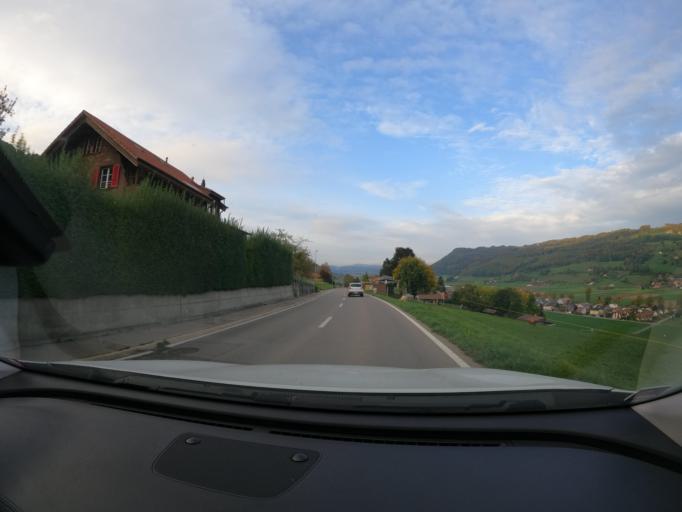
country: CH
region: Bern
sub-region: Bern-Mittelland District
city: Toffen
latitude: 46.8533
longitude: 7.4909
